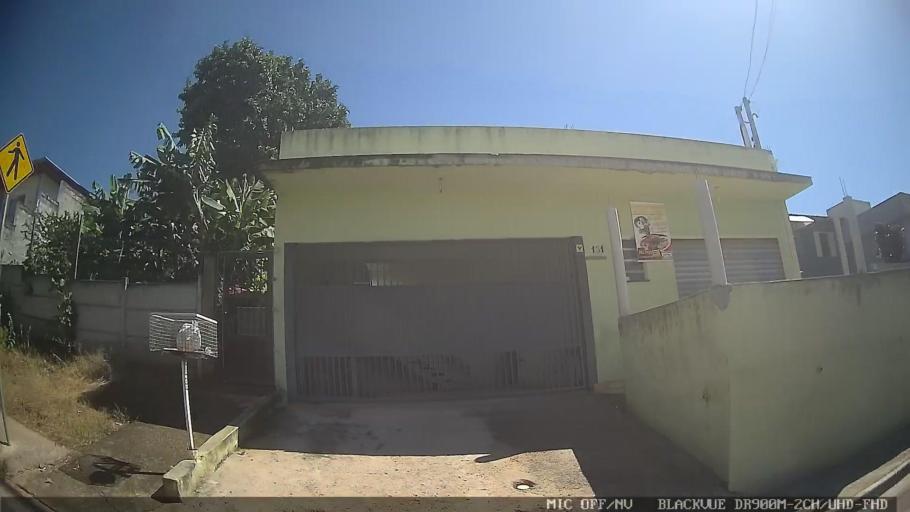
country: BR
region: Sao Paulo
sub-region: Atibaia
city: Atibaia
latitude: -23.1040
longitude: -46.5801
